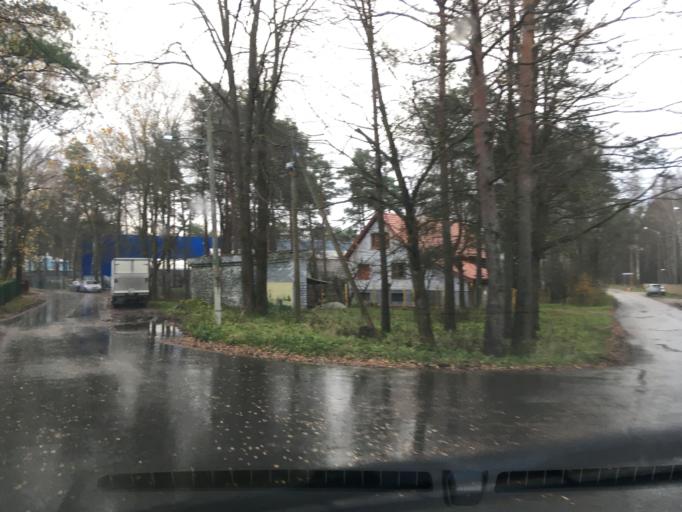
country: EE
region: Harju
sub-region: Tallinna linn
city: Tallinn
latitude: 59.3721
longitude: 24.7134
